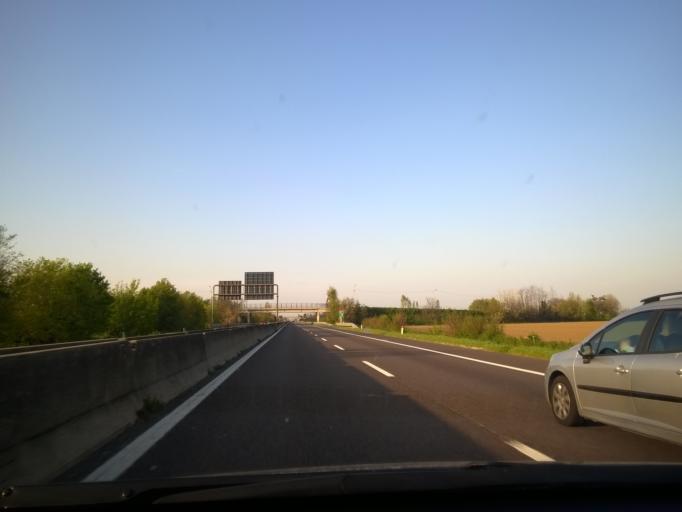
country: IT
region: Emilia-Romagna
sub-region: Provincia di Bologna
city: Progresso
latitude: 44.5464
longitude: 11.3706
